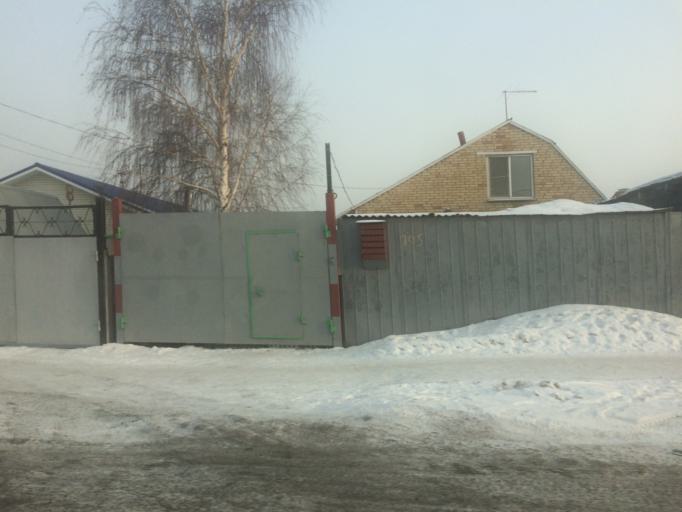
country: RU
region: Chelyabinsk
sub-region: Gorod Magnitogorsk
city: Magnitogorsk
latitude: 53.4298
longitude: 58.9619
